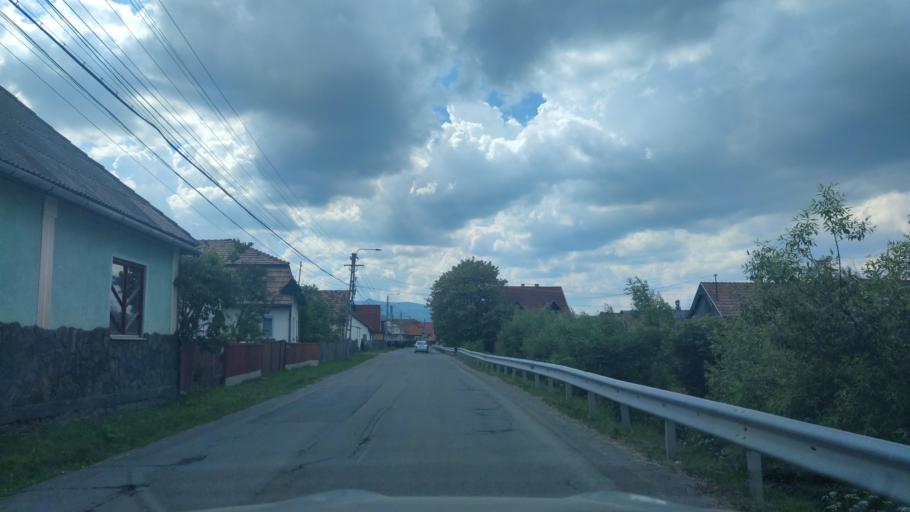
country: RO
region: Harghita
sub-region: Comuna Remetea
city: Remetea
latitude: 46.7948
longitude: 25.4372
